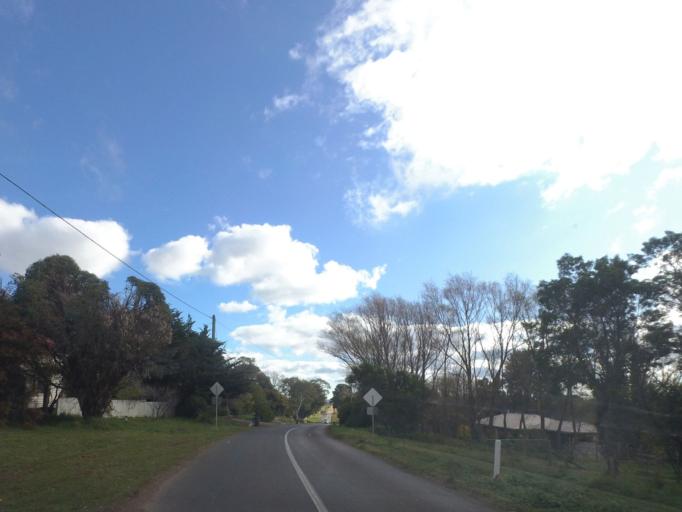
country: AU
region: Victoria
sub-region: Mount Alexander
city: Castlemaine
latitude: -37.2558
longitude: 144.4405
